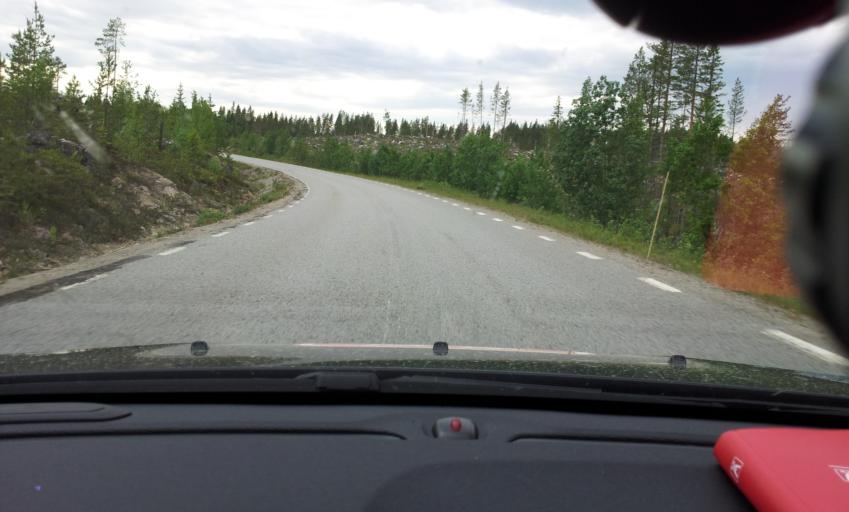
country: SE
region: Jaemtland
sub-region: Bergs Kommun
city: Hoverberg
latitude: 62.6775
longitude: 14.6951
